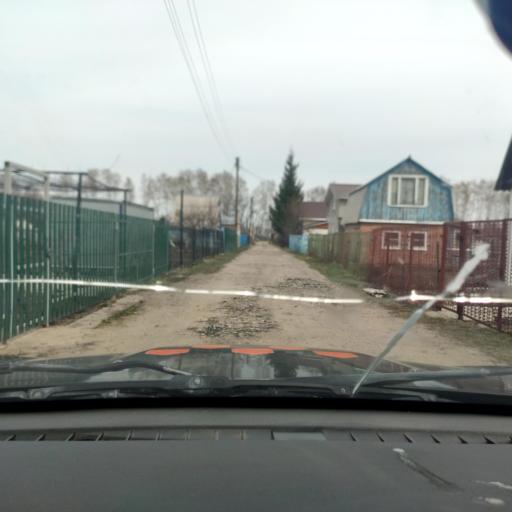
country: RU
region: Samara
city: Tol'yatti
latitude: 53.6034
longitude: 49.2465
